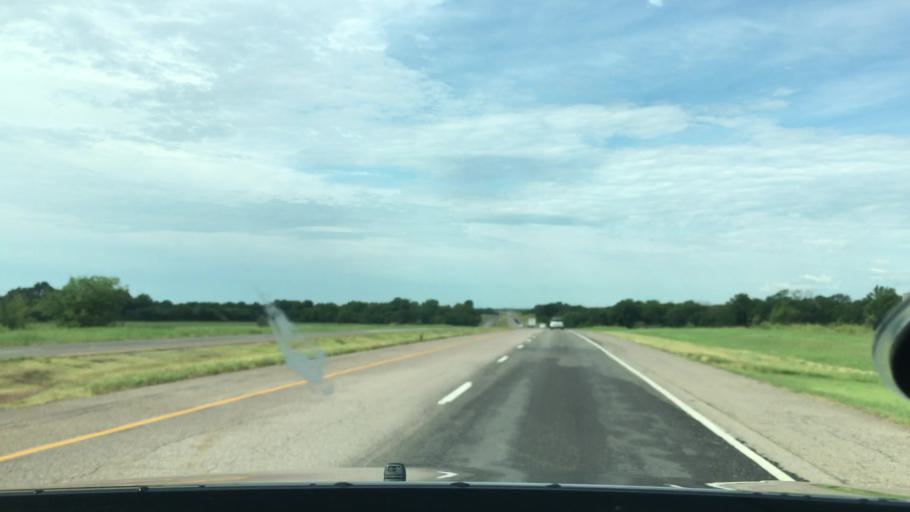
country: US
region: Oklahoma
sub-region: Pontotoc County
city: Ada
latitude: 34.6722
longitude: -96.7795
